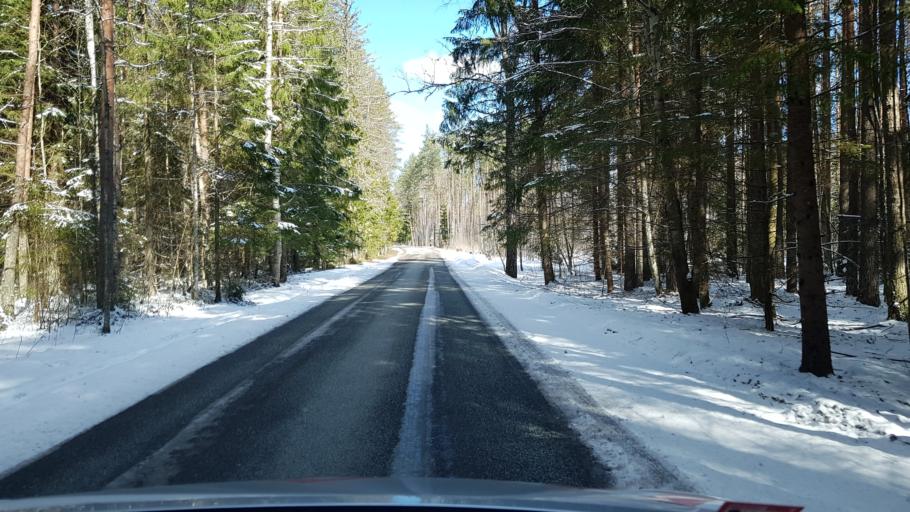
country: EE
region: Laeaene-Virumaa
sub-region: Kadrina vald
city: Kadrina
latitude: 59.5119
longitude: 25.9738
